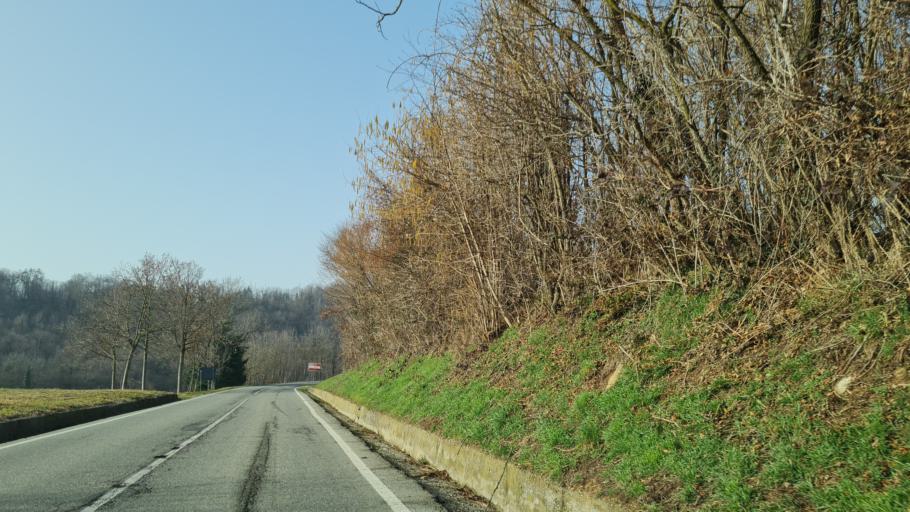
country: IT
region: Piedmont
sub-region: Provincia di Biella
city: Zimone
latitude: 45.4559
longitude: 8.0405
